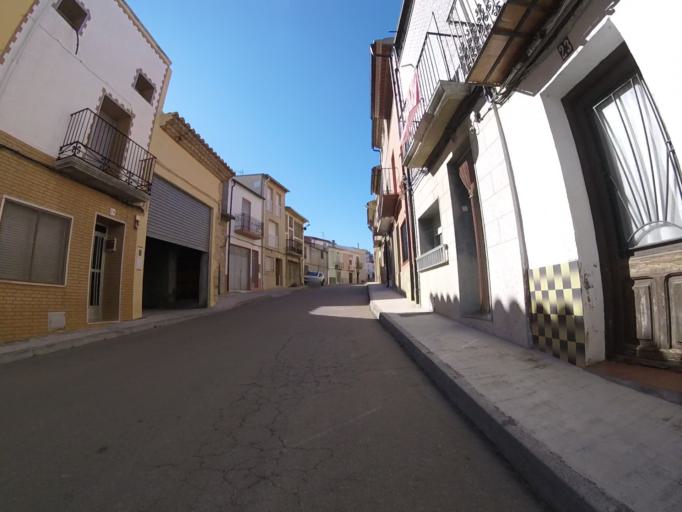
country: ES
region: Valencia
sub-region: Provincia de Castello
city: Cati
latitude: 40.4254
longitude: 0.0788
